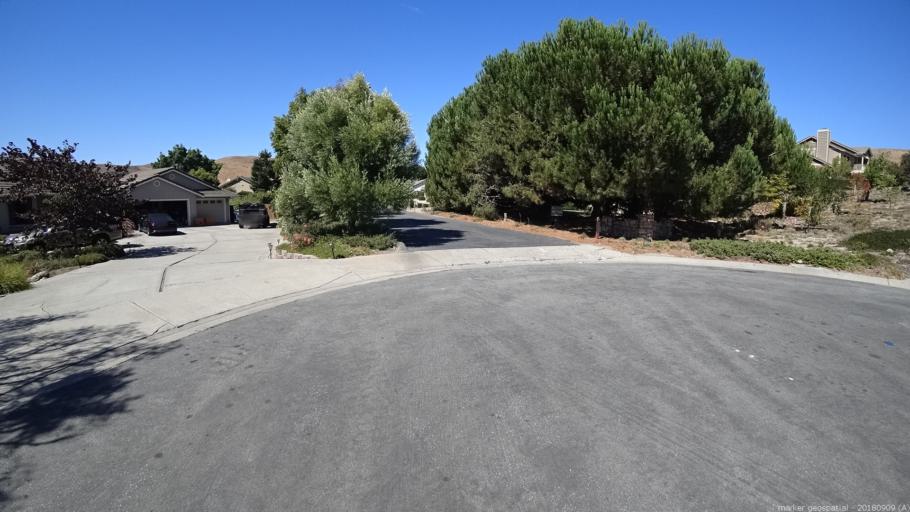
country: US
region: California
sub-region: Monterey County
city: Salinas
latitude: 36.6028
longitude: -121.7034
